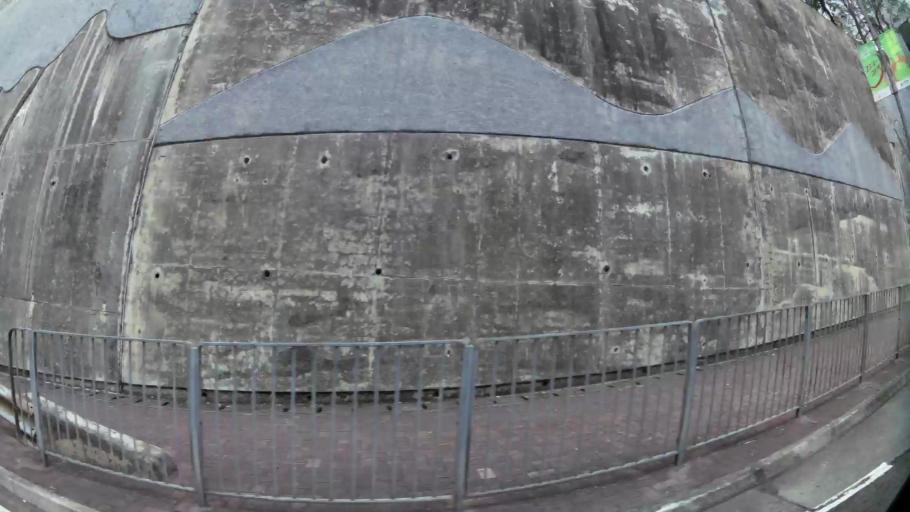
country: HK
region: Wanchai
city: Wan Chai
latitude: 22.2801
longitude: 114.2198
